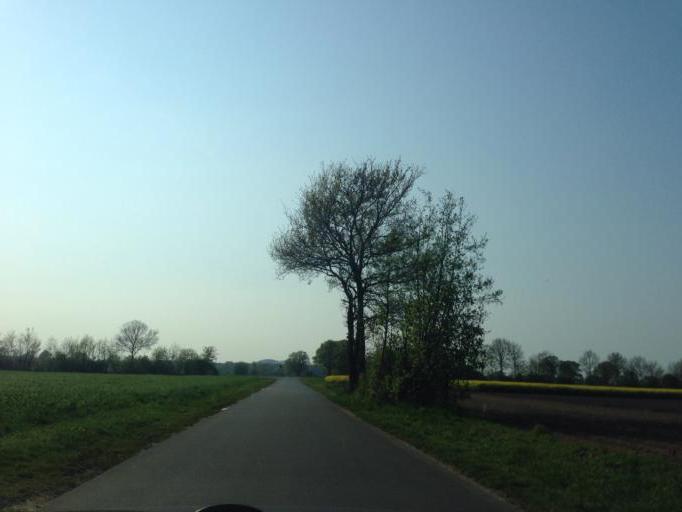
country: DE
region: Lower Saxony
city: Eicklingen
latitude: 52.5164
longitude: 10.1789
